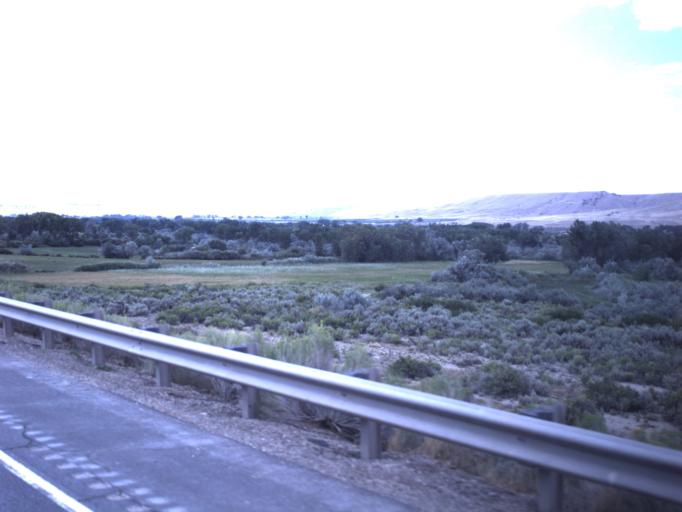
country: US
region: Utah
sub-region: Duchesne County
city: Duchesne
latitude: 40.1587
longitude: -110.2628
